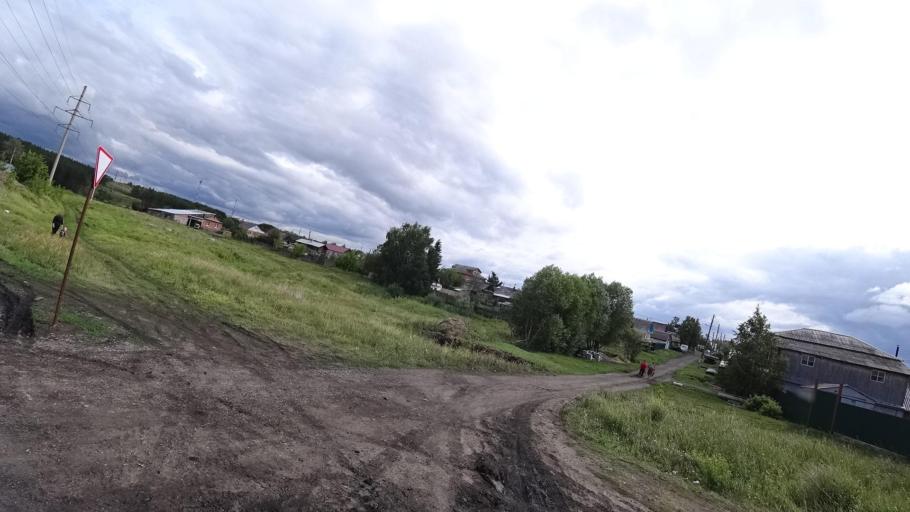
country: RU
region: Sverdlovsk
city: Kamyshlov
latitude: 56.8637
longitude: 62.7109
